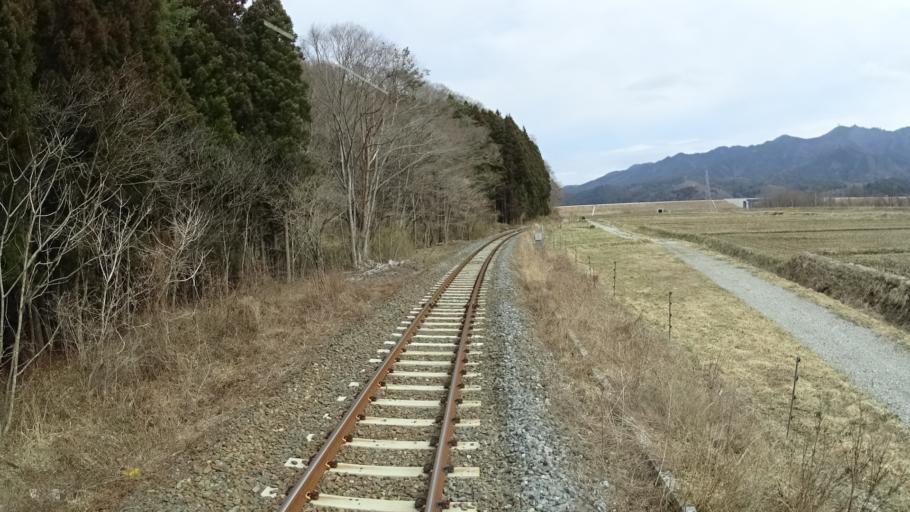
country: JP
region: Iwate
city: Yamada
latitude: 39.5227
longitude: 141.9180
